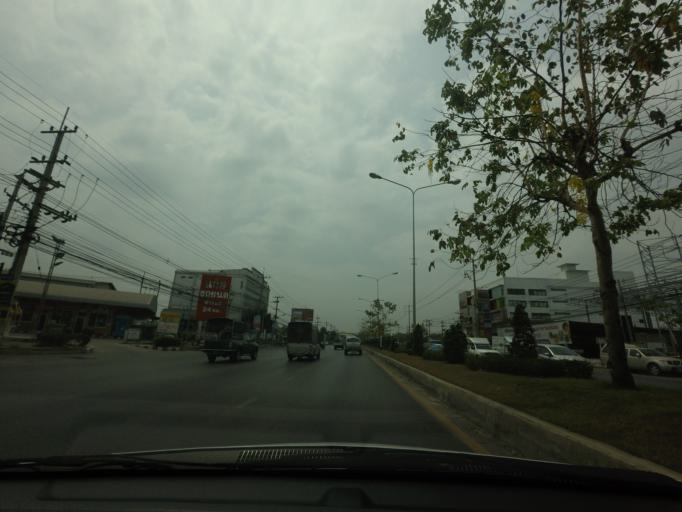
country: TH
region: Bangkok
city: Nong Khaem
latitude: 13.7363
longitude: 100.3296
